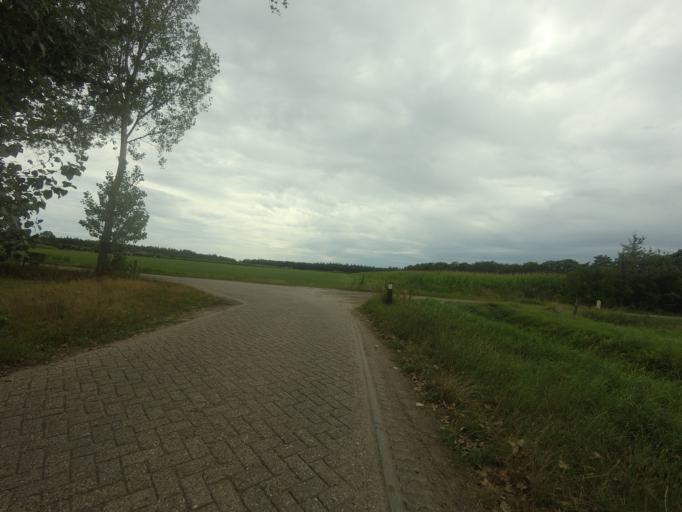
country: NL
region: Overijssel
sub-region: Gemeente Raalte
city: Raalte
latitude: 52.3548
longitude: 6.3176
